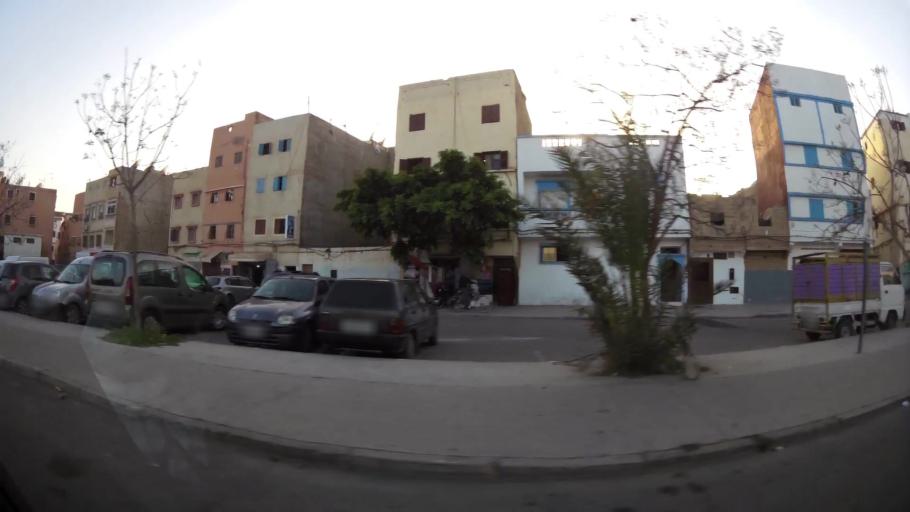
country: MA
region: Oued ed Dahab-Lagouira
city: Dakhla
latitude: 30.3895
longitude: -9.5665
